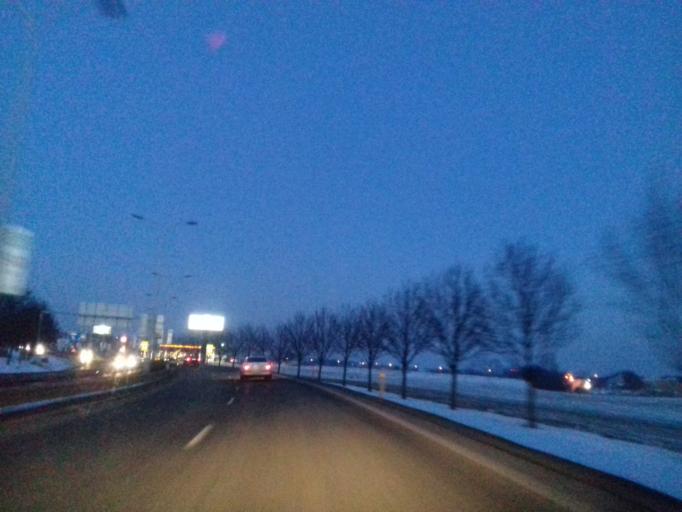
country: CZ
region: Central Bohemia
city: Tuchomerice
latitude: 50.1104
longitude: 14.2794
